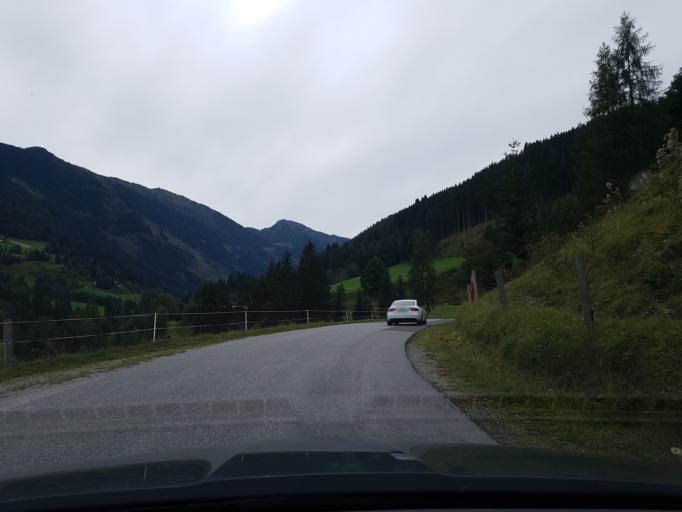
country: AT
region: Salzburg
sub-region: Politischer Bezirk Sankt Johann im Pongau
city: Forstau
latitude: 47.3680
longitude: 13.5540
